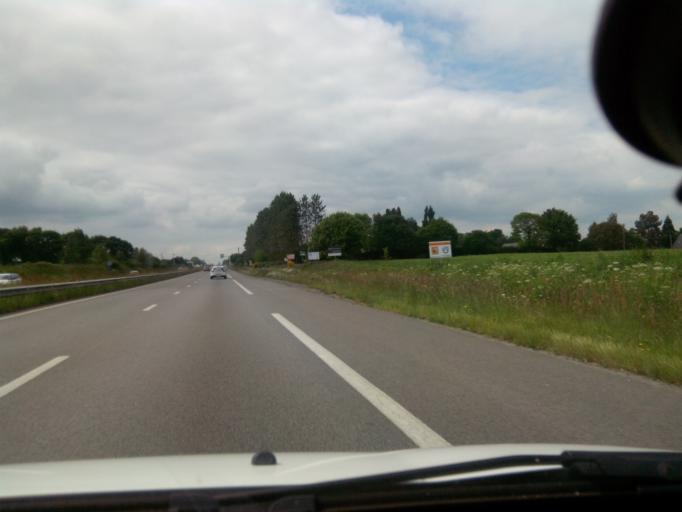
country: FR
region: Brittany
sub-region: Departement d'Ille-et-Vilaine
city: Pleumeleuc
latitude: 48.1725
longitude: -1.9152
